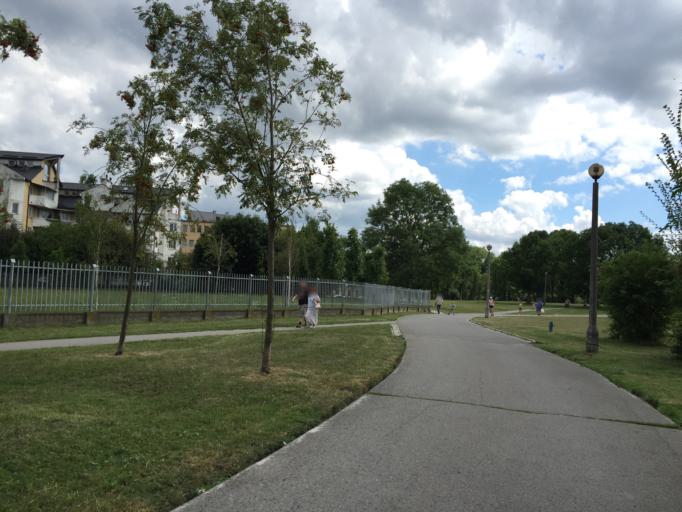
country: PL
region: Lesser Poland Voivodeship
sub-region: Powiat wielicki
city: Kokotow
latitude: 50.0679
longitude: 20.0408
